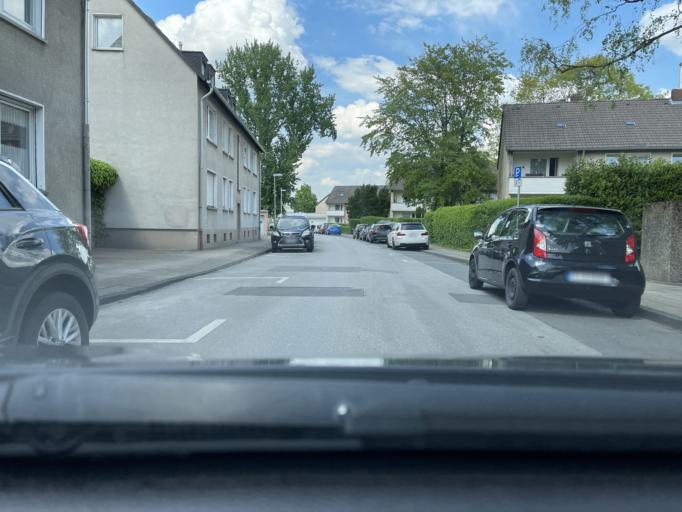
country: DE
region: North Rhine-Westphalia
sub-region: Regierungsbezirk Munster
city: Bottrop
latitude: 51.4780
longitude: 6.9287
